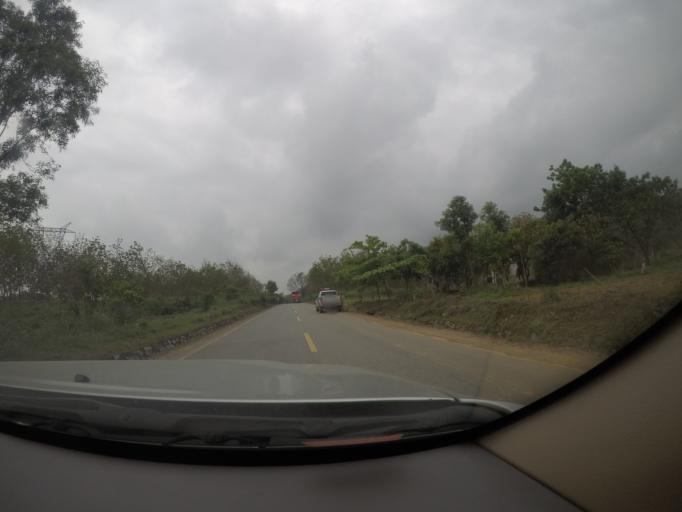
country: VN
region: Quang Binh
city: Hoan Lao
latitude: 17.5661
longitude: 106.4428
